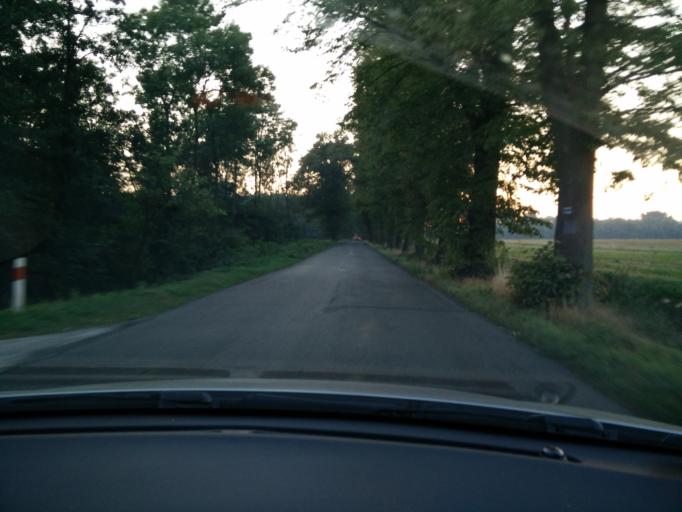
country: PL
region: Greater Poland Voivodeship
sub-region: Powiat wrzesinski
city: Miloslaw
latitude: 52.2050
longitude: 17.4605
